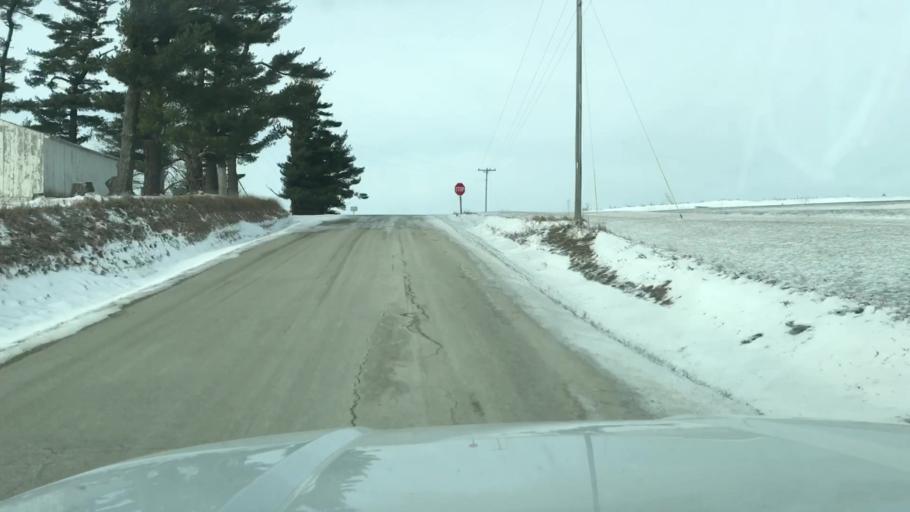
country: US
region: Missouri
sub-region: Holt County
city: Mound City
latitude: 40.1301
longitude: -95.0898
